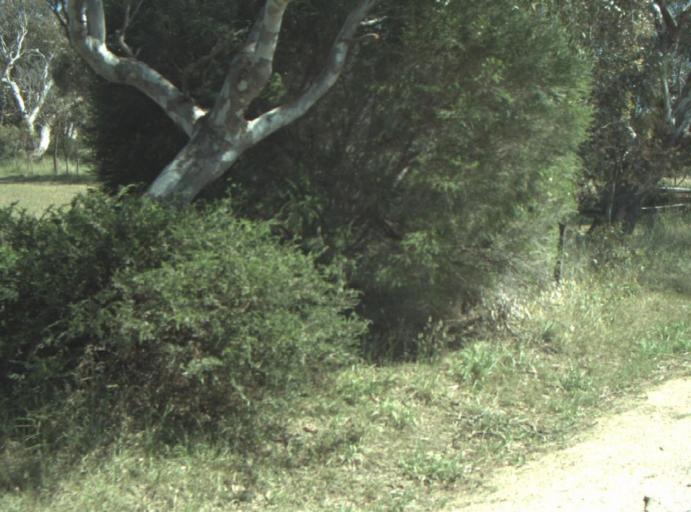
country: AU
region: Victoria
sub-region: Greater Geelong
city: Breakwater
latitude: -38.2400
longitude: 144.3528
